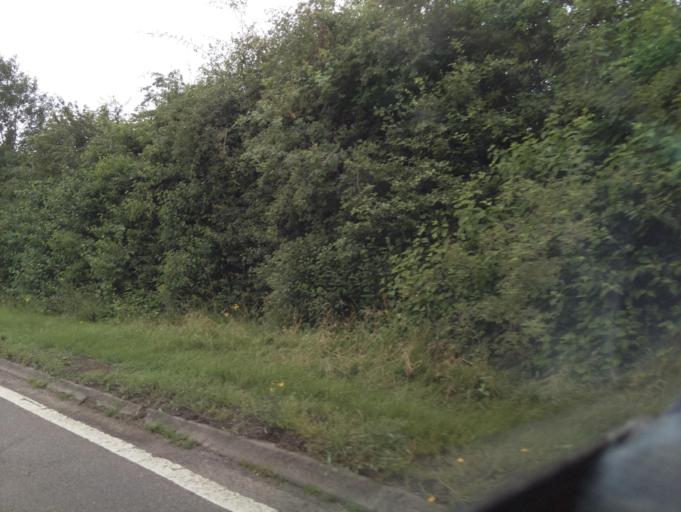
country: GB
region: England
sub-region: Northamptonshire
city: Corby
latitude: 52.4879
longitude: -0.7326
